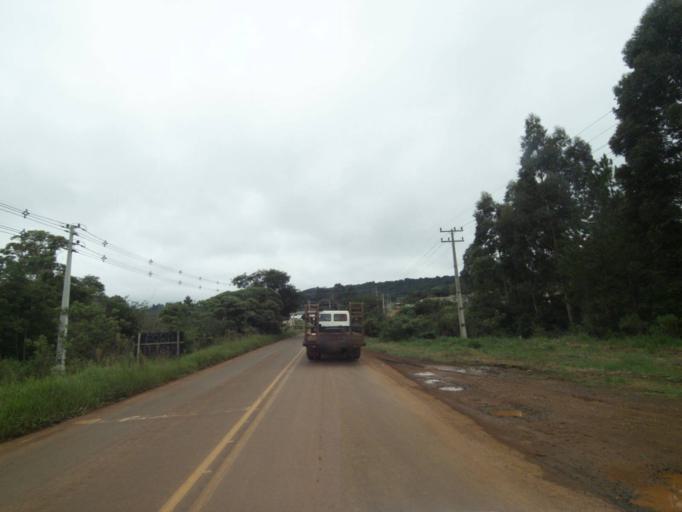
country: BR
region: Parana
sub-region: Pitanga
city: Pitanga
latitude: -24.9272
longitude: -51.8740
